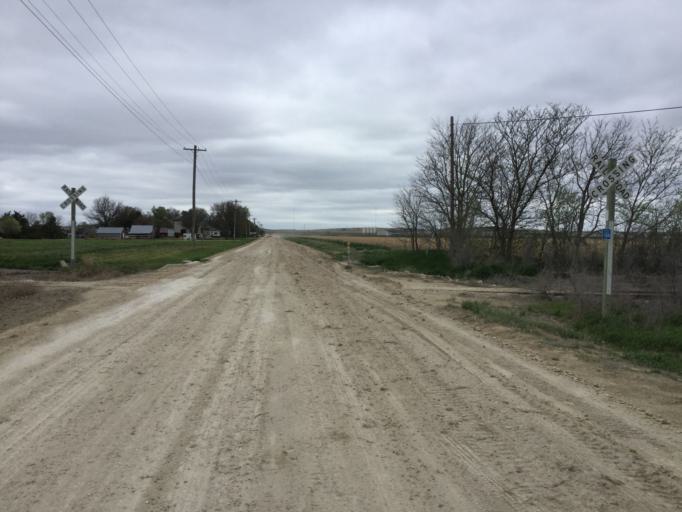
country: US
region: Kansas
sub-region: Osborne County
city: Osborne
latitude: 39.4439
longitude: -98.7040
